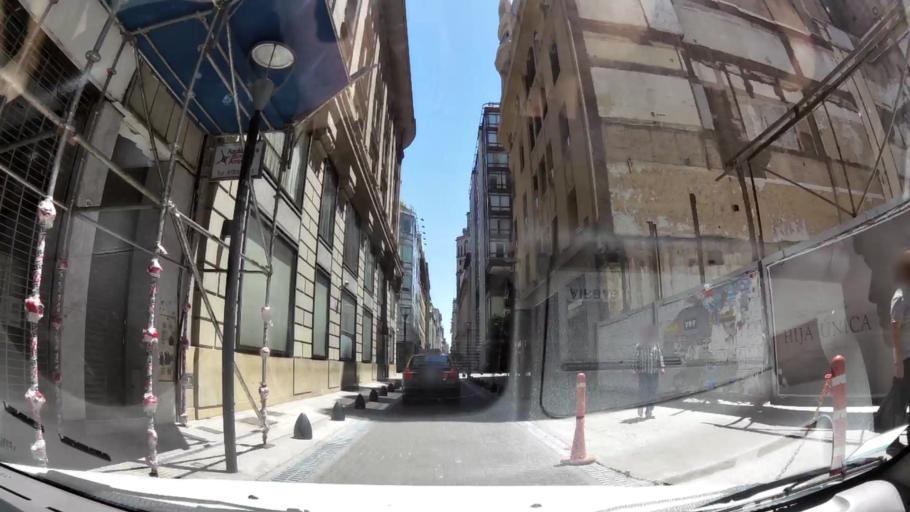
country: AR
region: Buenos Aires F.D.
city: Buenos Aires
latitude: -34.6056
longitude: -58.3734
